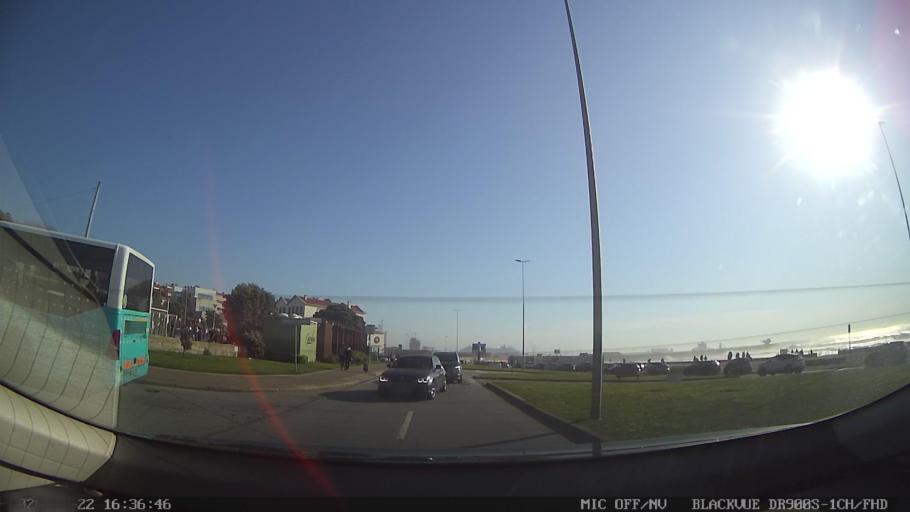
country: PT
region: Porto
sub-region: Matosinhos
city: Leca da Palmeira
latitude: 41.1910
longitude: -8.7052
